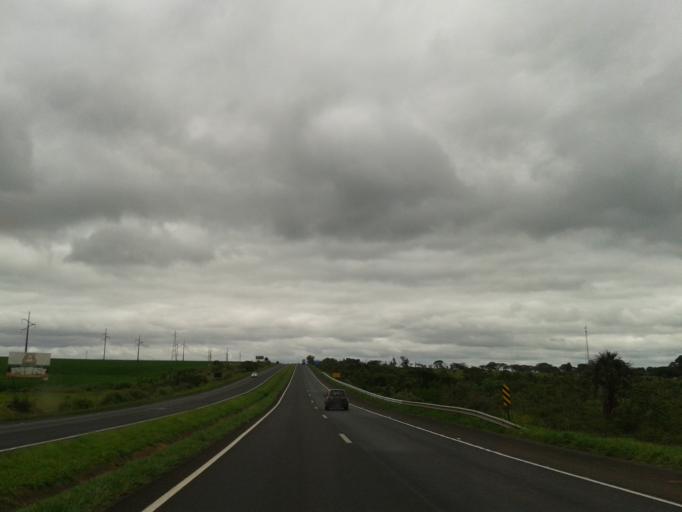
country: BR
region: Minas Gerais
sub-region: Uberlandia
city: Uberlandia
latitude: -19.0319
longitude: -48.2018
